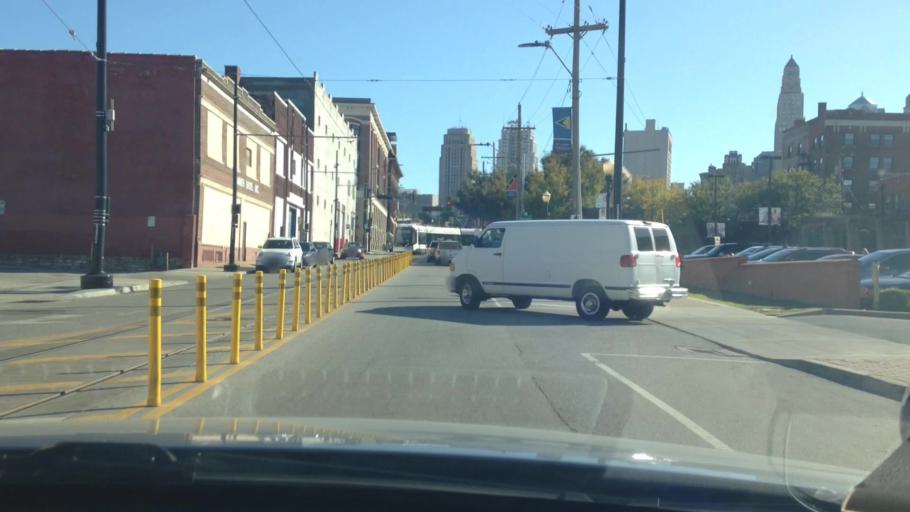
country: US
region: Missouri
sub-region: Jackson County
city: Kansas City
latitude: 39.1099
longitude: -94.5809
